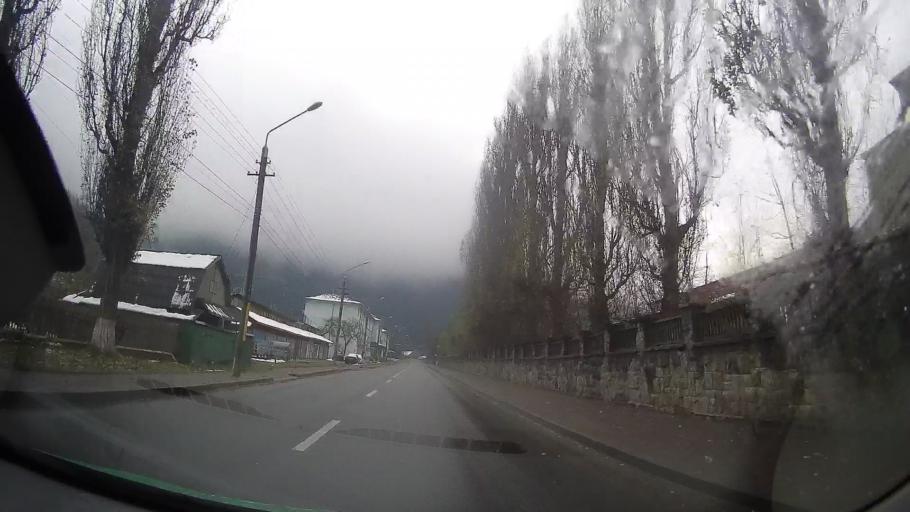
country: RO
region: Neamt
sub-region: Comuna Bicaz
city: Bicaz
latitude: 46.9041
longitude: 26.0750
